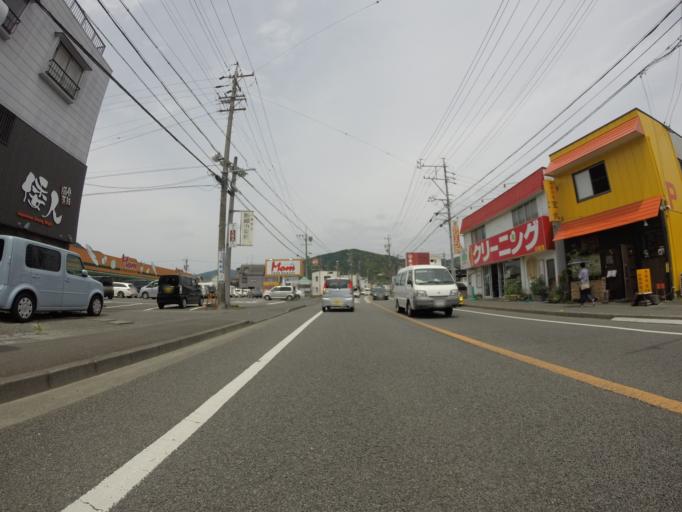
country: JP
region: Shizuoka
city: Shizuoka-shi
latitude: 34.9818
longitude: 138.3374
